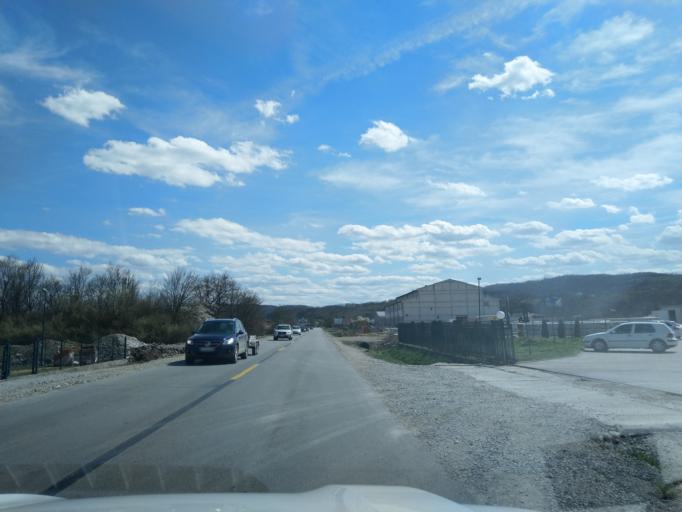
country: RS
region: Central Serbia
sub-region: Zlatiborski Okrug
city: Arilje
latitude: 43.8002
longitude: 20.0960
